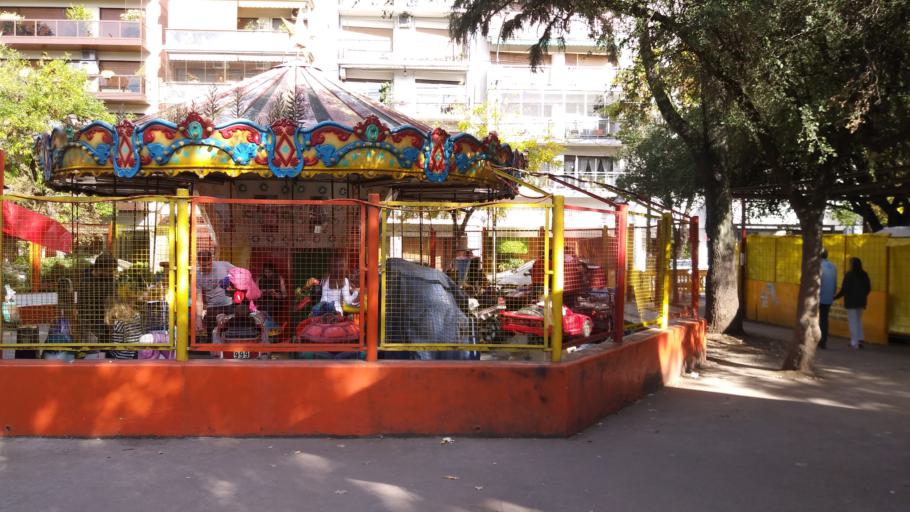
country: AR
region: Buenos Aires F.D.
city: Villa Santa Rita
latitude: -34.6188
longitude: -58.4342
